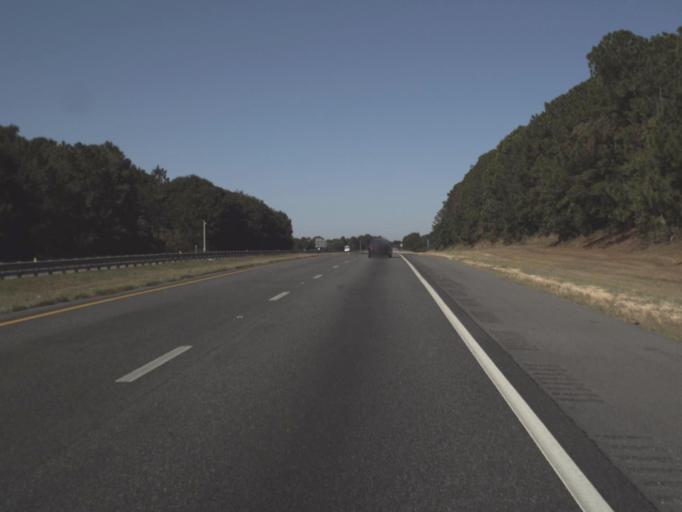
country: US
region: Florida
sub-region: Orange County
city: Oakland
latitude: 28.5568
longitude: -81.6714
